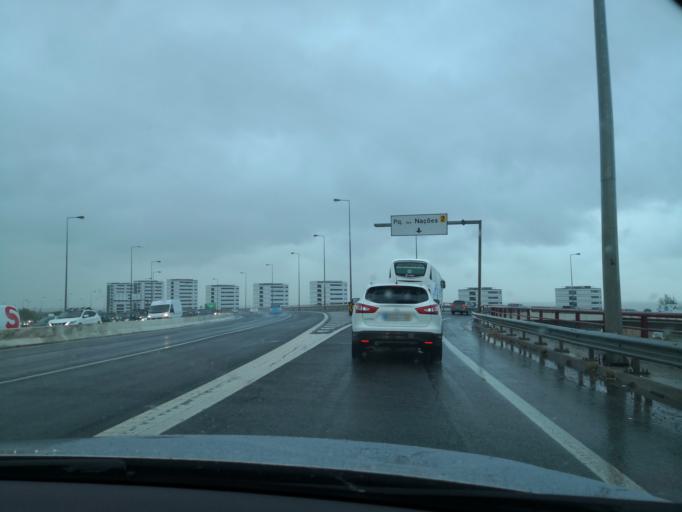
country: PT
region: Lisbon
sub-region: Loures
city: Sacavem
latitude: 38.7887
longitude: -9.1021
